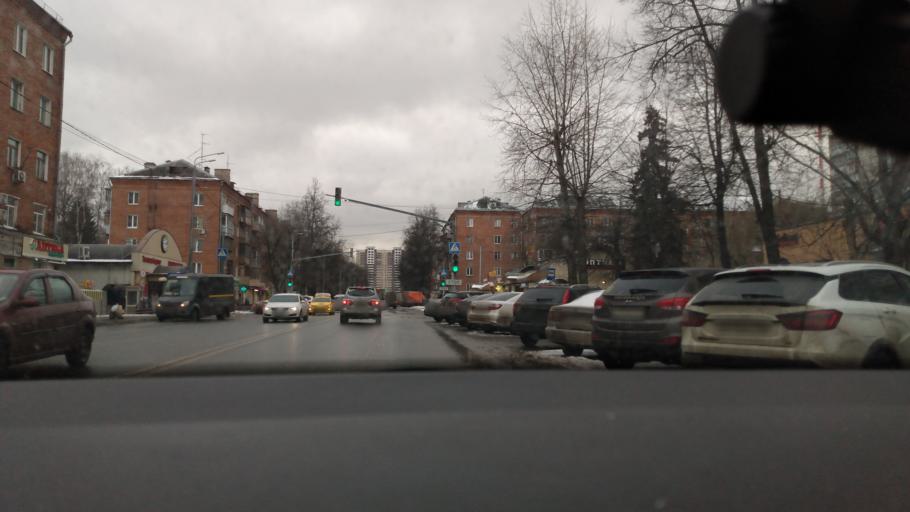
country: RU
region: Moskovskaya
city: Balashikha
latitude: 55.8005
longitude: 37.9347
